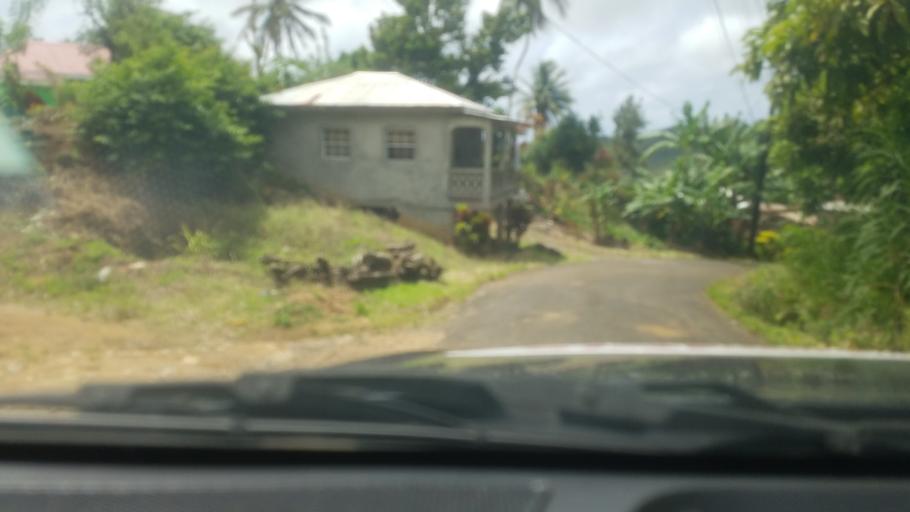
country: LC
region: Micoud Quarter
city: Micoud
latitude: 13.8032
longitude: -60.9493
